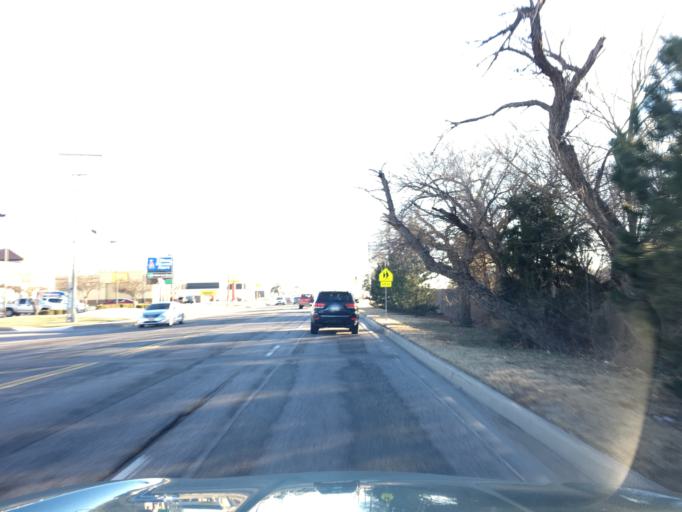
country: US
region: Kansas
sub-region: Sedgwick County
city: Bellaire
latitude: 37.6992
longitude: -97.2263
